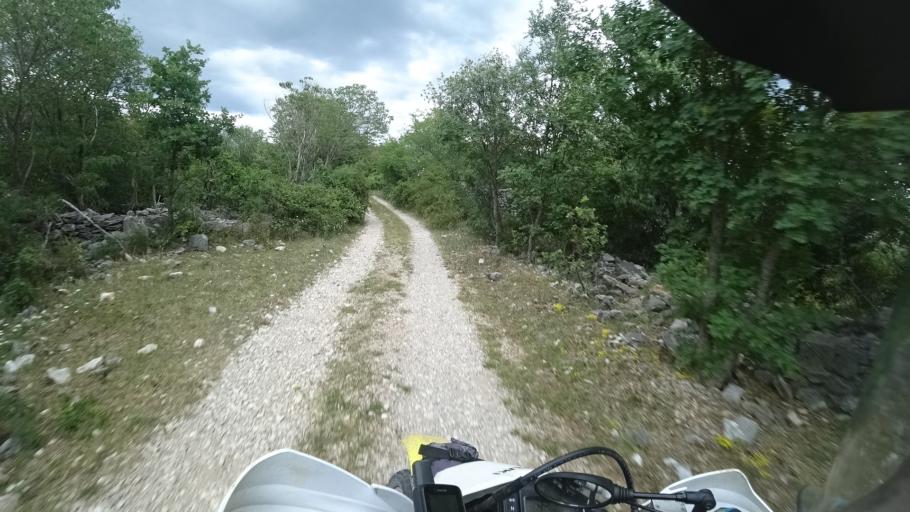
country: HR
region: Zadarska
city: Gracac
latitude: 44.1551
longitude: 15.9346
